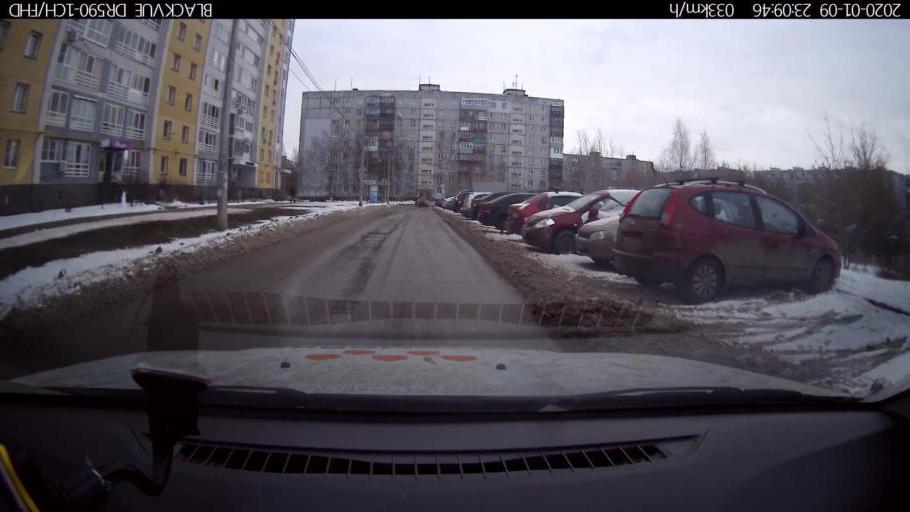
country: RU
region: Nizjnij Novgorod
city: Gorbatovka
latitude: 56.3667
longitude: 43.8081
